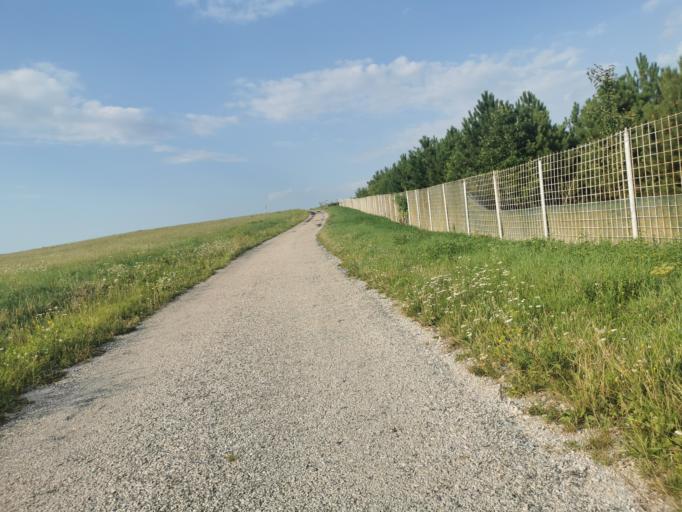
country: SK
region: Trenciansky
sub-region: Okres Myjava
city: Myjava
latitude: 48.7912
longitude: 17.5705
